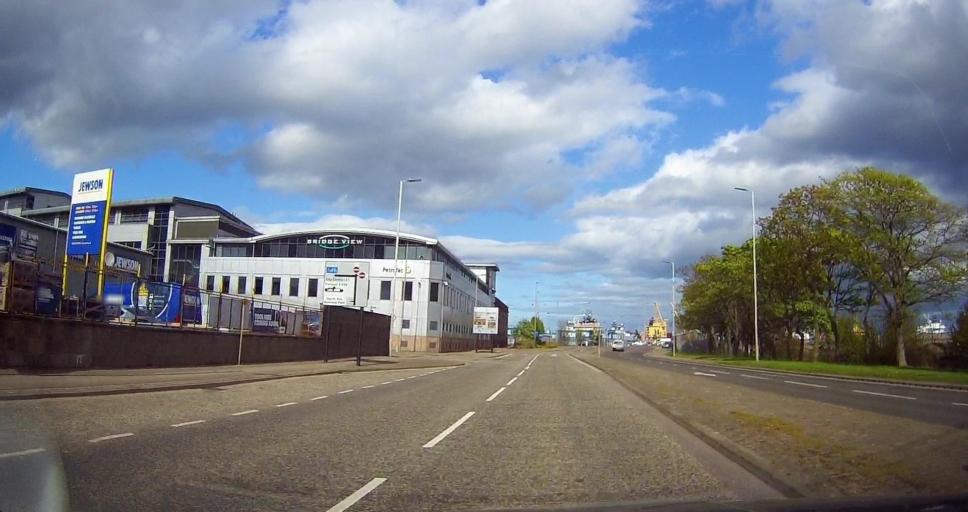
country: GB
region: Scotland
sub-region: Aberdeen City
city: Aberdeen
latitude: 57.1400
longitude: -2.0927
